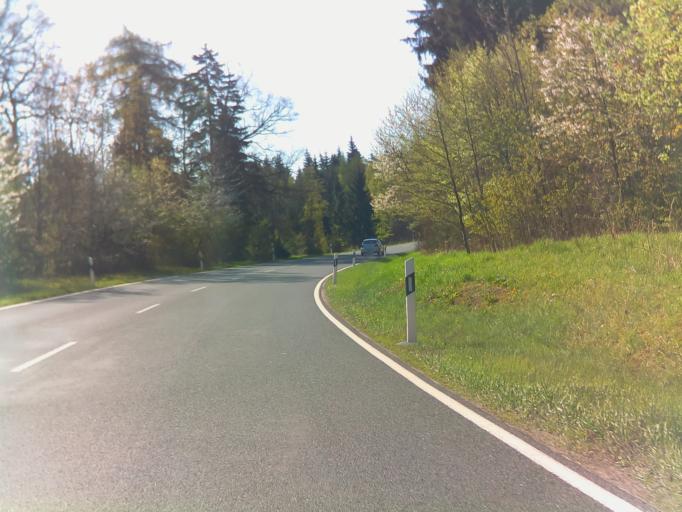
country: DE
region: Thuringia
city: Tanna
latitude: 50.5445
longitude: 11.8583
